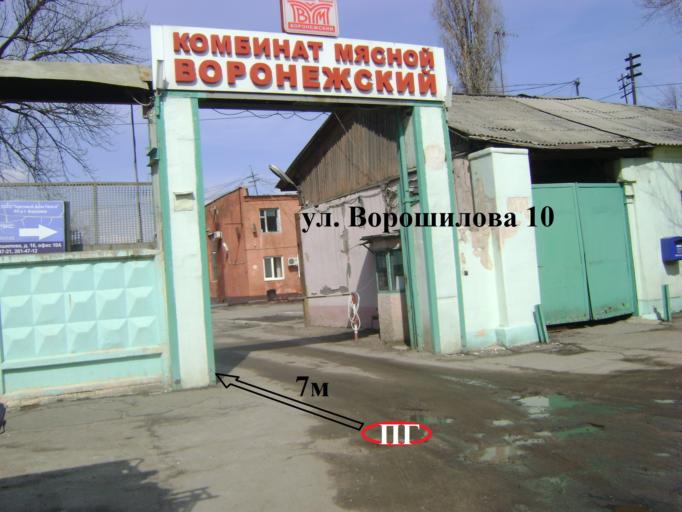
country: RU
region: Voronezj
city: Voronezh
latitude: 51.6562
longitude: 39.1805
